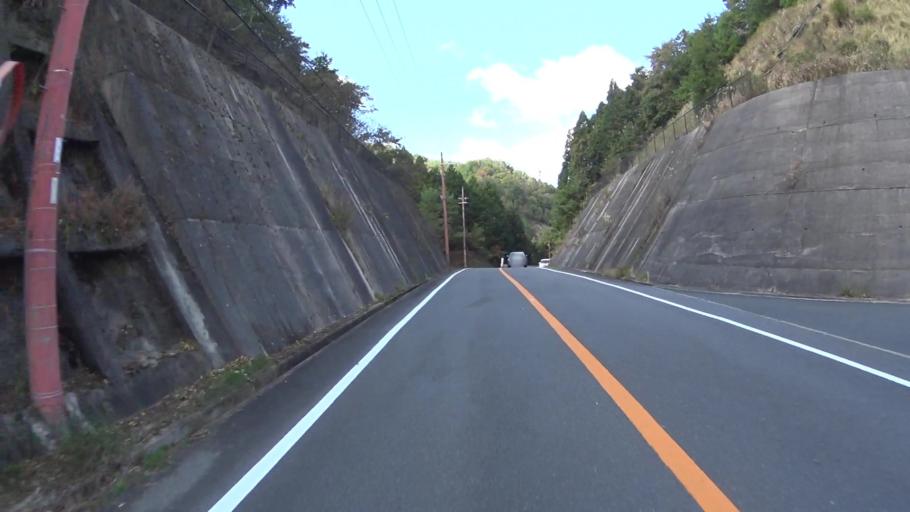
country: JP
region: Kyoto
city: Kameoka
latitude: 35.1314
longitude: 135.5395
